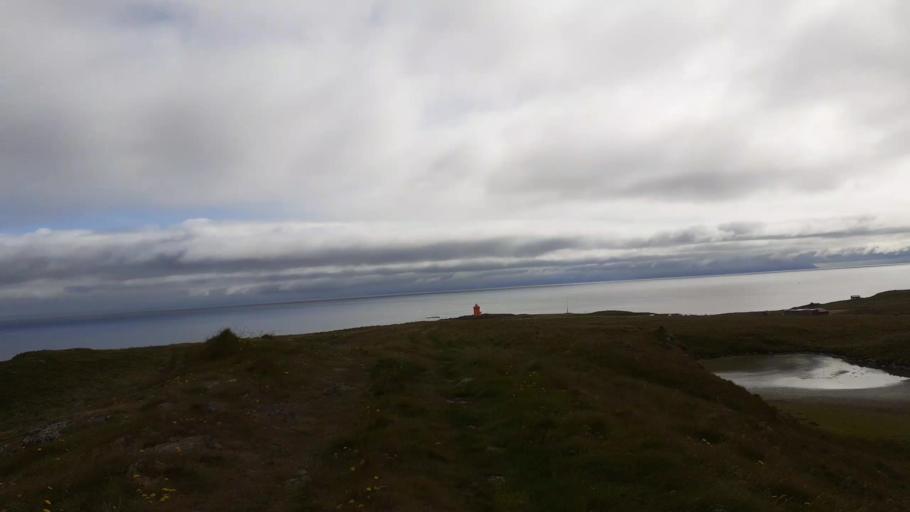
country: IS
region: Northeast
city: Dalvik
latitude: 66.5330
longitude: -17.9828
